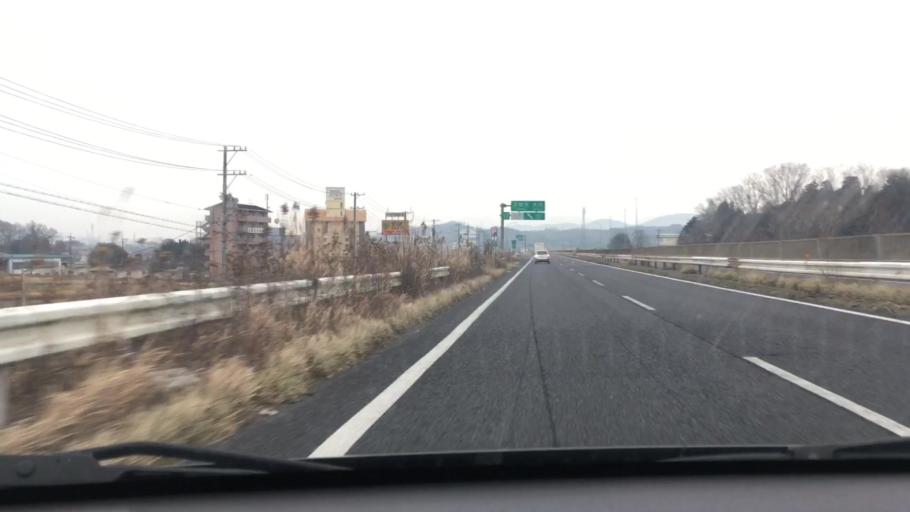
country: JP
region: Mie
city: Ueno-ebisumachi
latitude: 34.7373
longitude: 136.1070
